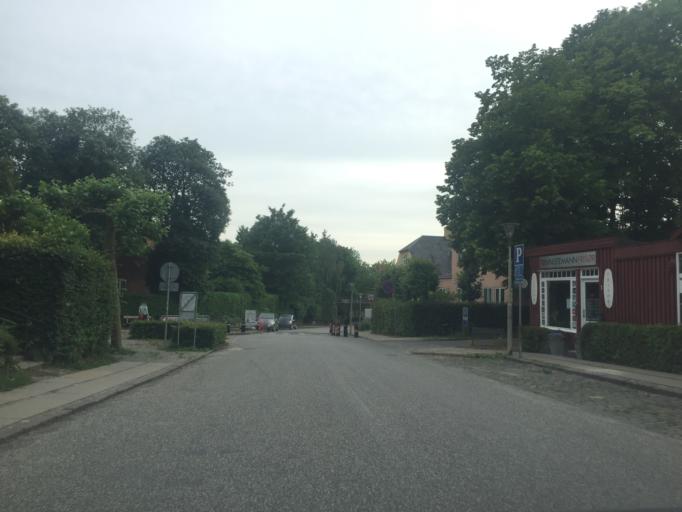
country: DK
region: Capital Region
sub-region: Lyngby-Tarbaek Kommune
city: Kongens Lyngby
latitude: 55.7759
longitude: 12.5031
